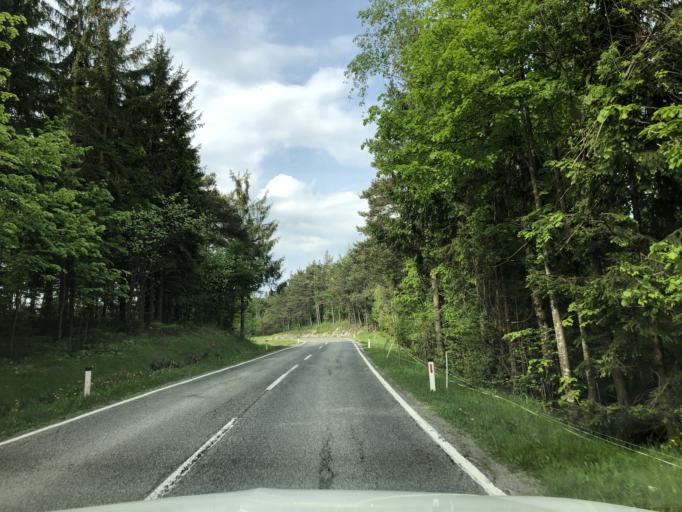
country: SI
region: Bloke
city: Nova Vas
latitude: 45.7696
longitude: 14.4829
